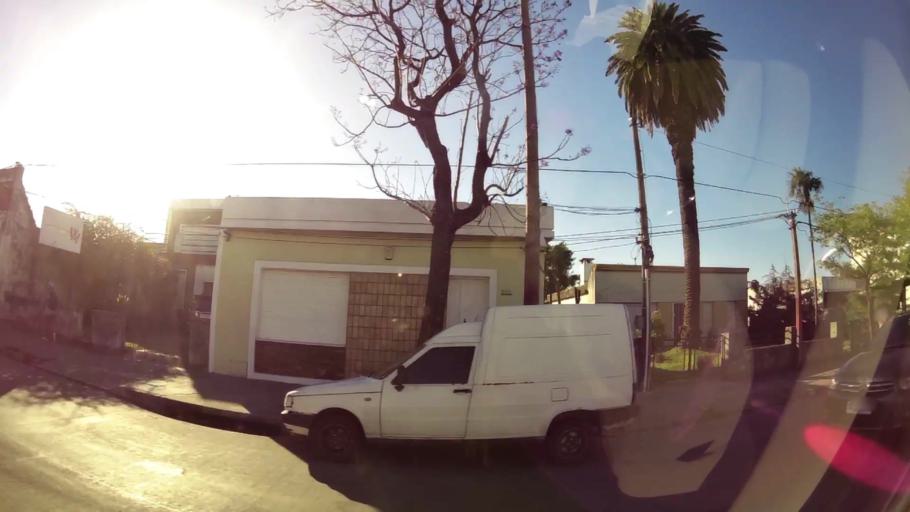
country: UY
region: Canelones
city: La Paz
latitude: -34.8316
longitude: -56.2146
